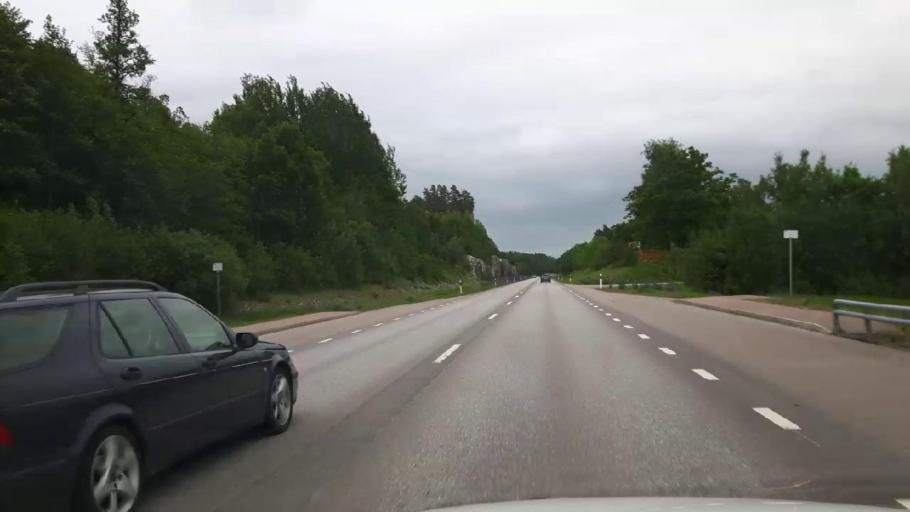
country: SE
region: Vaestmanland
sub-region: Kopings Kommun
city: Kolsva
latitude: 59.5670
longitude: 15.8826
